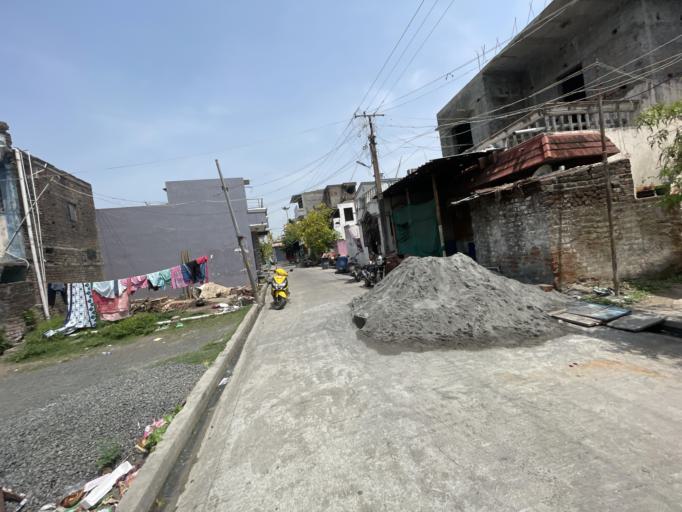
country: IN
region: Tamil Nadu
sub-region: Villupuram
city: Auroville
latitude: 11.9773
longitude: 79.7225
